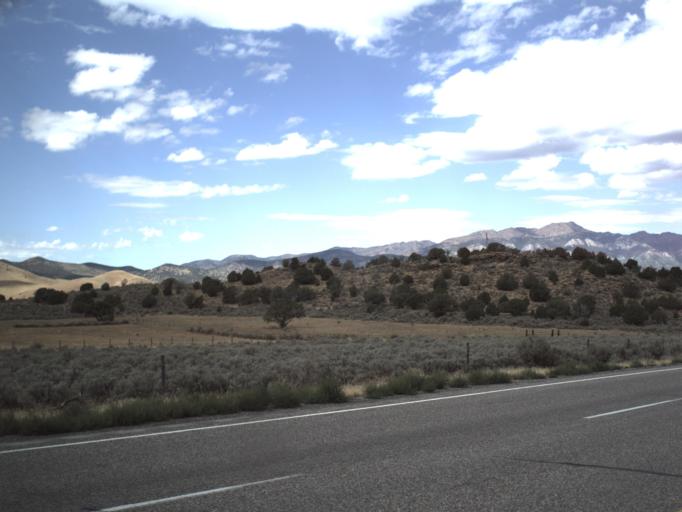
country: US
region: Utah
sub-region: Sanpete County
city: Gunnison
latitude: 39.2031
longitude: -112.0872
